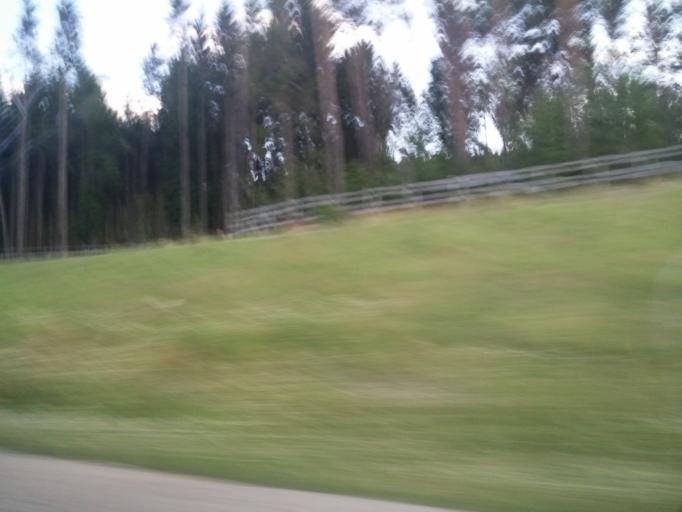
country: DE
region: Bavaria
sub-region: Regierungsbezirk Unterfranken
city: Geiselwind
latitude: 49.7807
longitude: 10.4467
